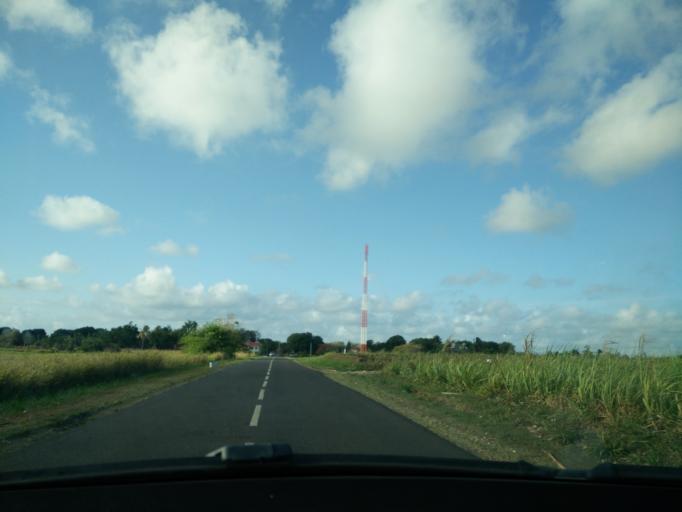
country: GP
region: Guadeloupe
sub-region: Guadeloupe
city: Le Moule
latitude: 16.3046
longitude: -61.3670
